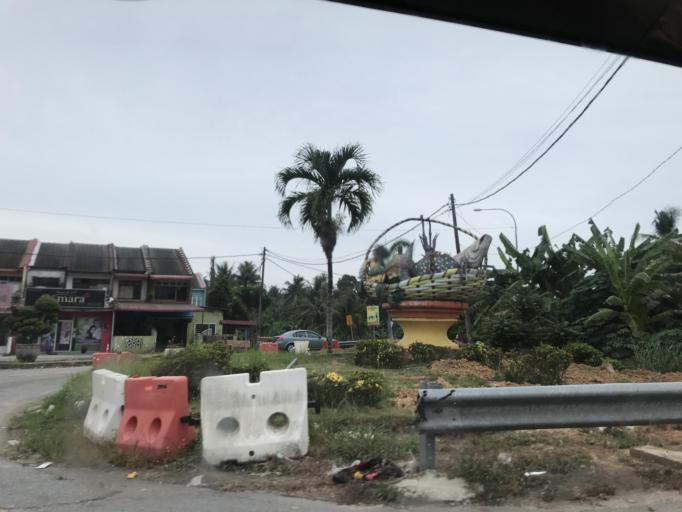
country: MY
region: Kelantan
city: Kota Bharu
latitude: 6.1213
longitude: 102.2065
